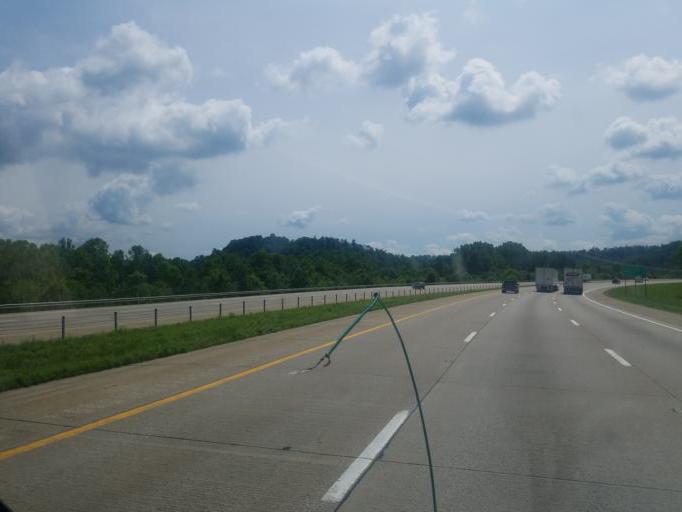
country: US
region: Kentucky
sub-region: Bullitt County
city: Lebanon Junction
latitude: 37.7928
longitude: -85.7556
